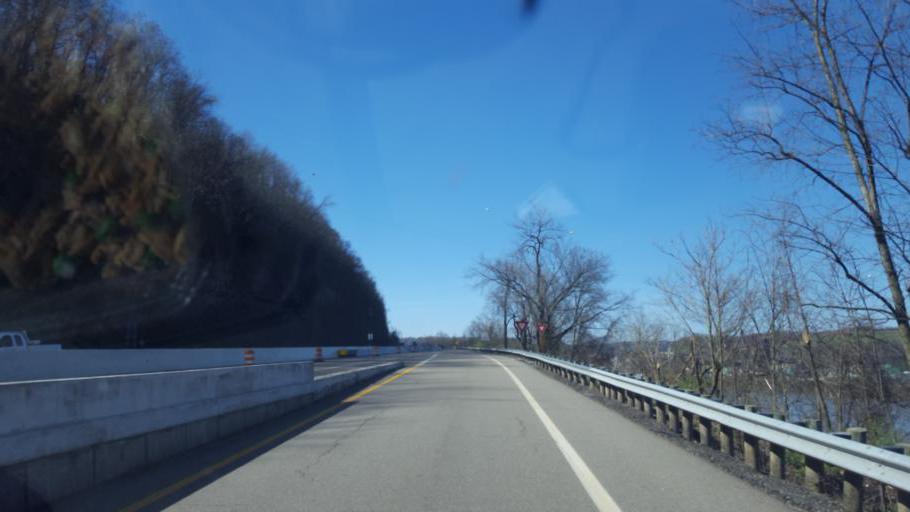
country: US
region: Ohio
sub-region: Jefferson County
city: Mingo Junction
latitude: 40.3287
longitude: -80.6059
